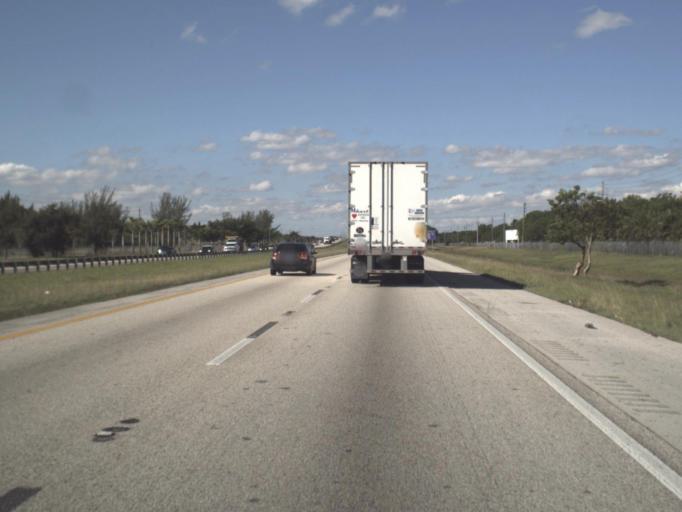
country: US
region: Florida
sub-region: Miami-Dade County
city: Lake Lucerne
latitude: 25.9718
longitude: -80.2712
